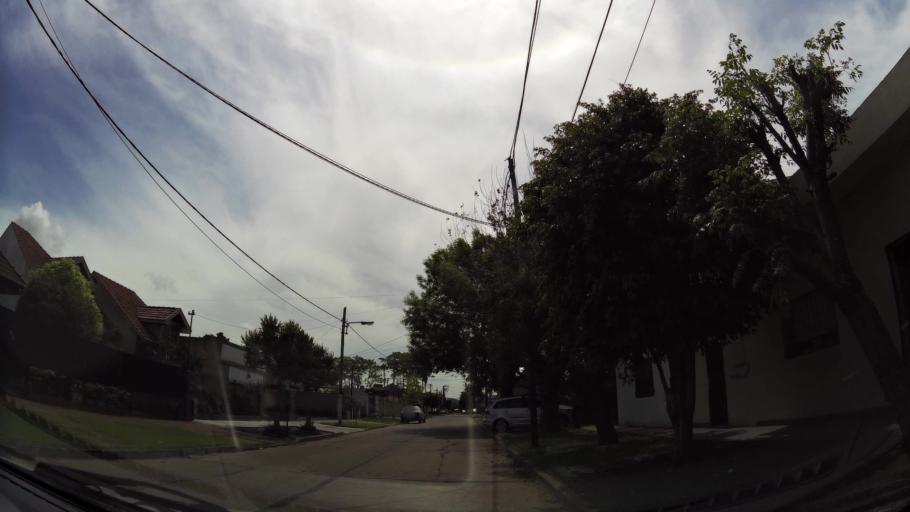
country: AR
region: Buenos Aires
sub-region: Partido de Quilmes
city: Quilmes
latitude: -34.7811
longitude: -58.2661
